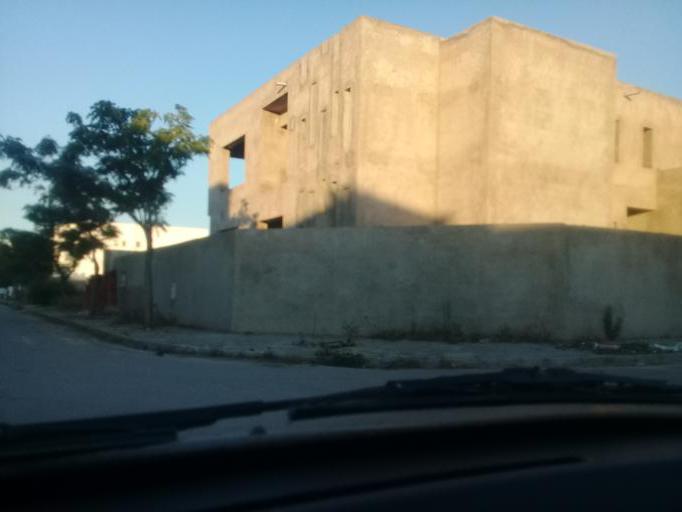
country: TN
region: Tunis
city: La Goulette
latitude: 36.8451
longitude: 10.2650
